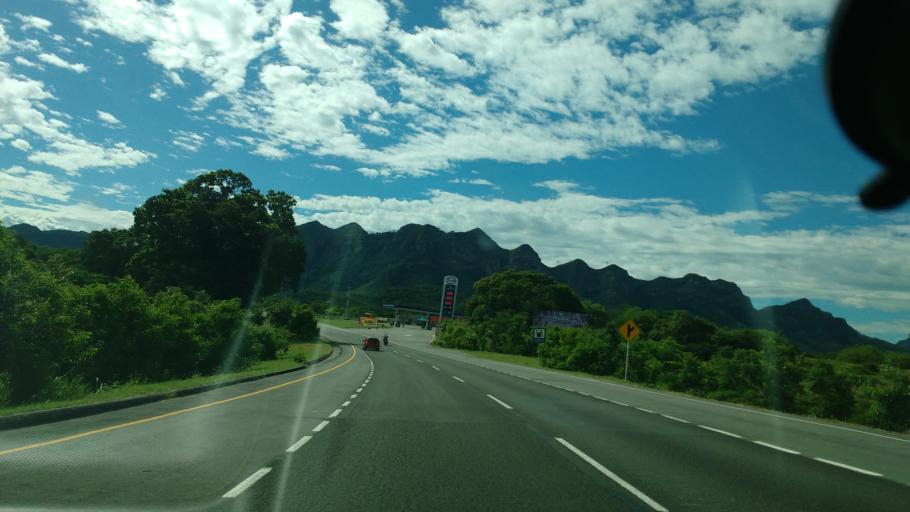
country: CO
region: Tolima
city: Valle de San Juan
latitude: 4.2701
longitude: -74.9993
